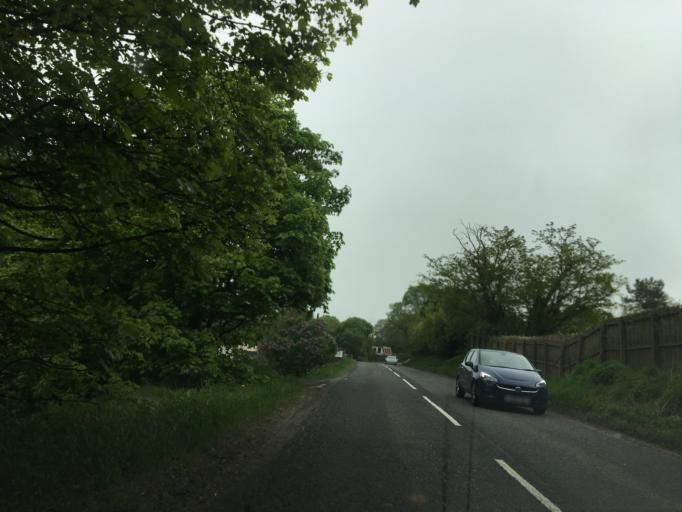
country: GB
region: Scotland
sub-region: The Scottish Borders
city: West Linton
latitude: 55.7243
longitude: -3.3285
